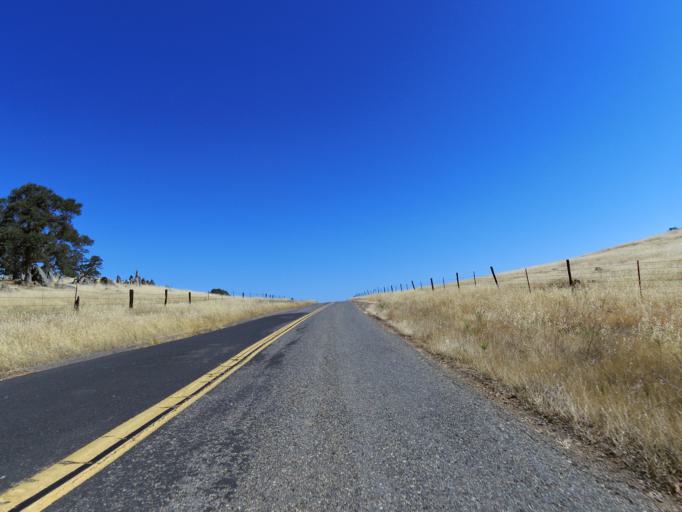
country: US
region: California
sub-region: Merced County
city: Planada
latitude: 37.5623
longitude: -120.3260
